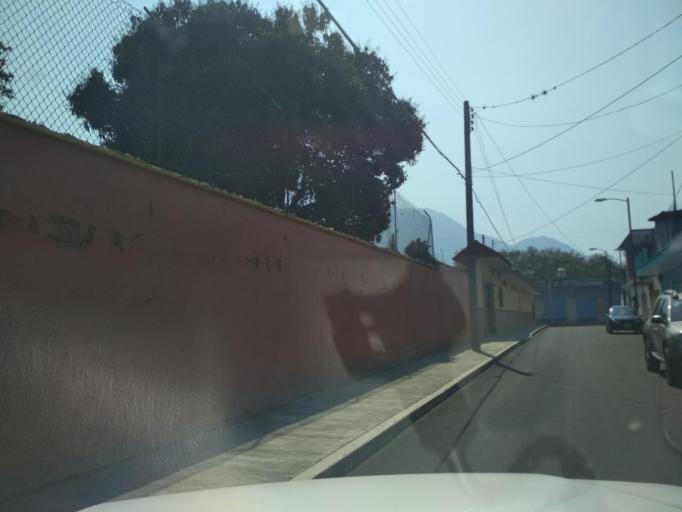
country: MX
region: Veracruz
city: Orizaba
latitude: 18.8404
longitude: -97.0971
